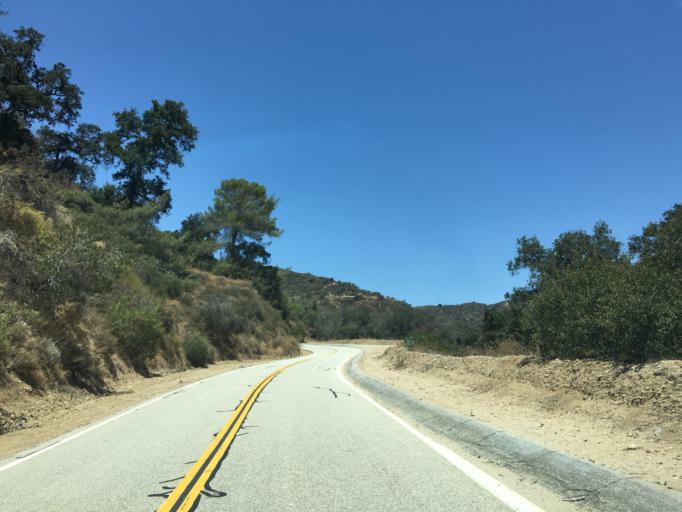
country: US
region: California
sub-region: Los Angeles County
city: Glendora
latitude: 34.1604
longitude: -117.8428
